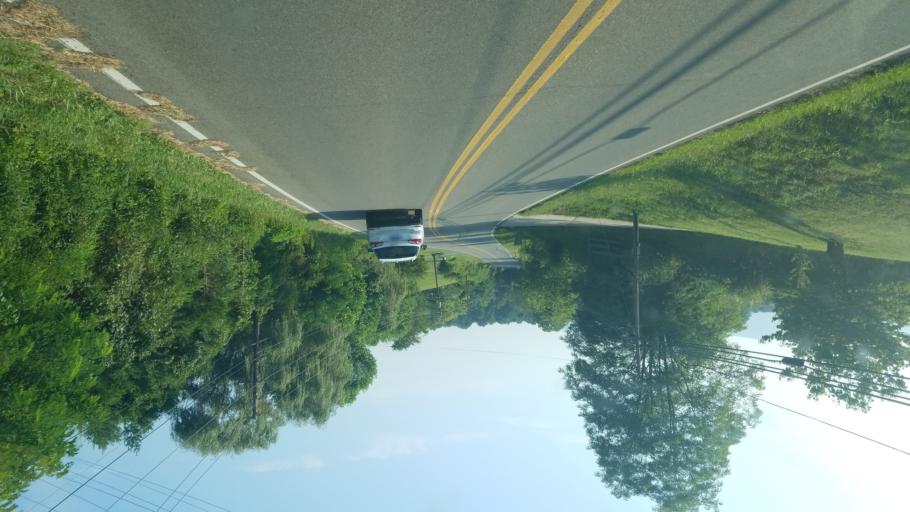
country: US
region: Tennessee
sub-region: Sullivan County
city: Bluff City
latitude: 36.4850
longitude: -82.2641
